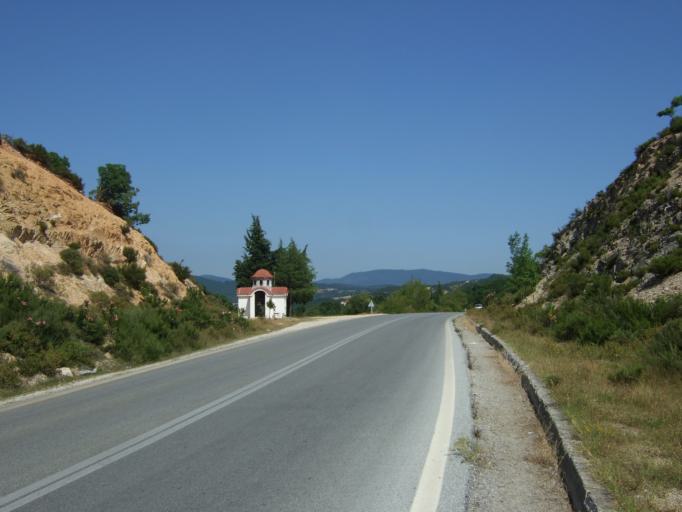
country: GR
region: Central Macedonia
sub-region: Nomos Chalkidikis
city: Arnaia
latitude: 40.5039
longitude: 23.5531
